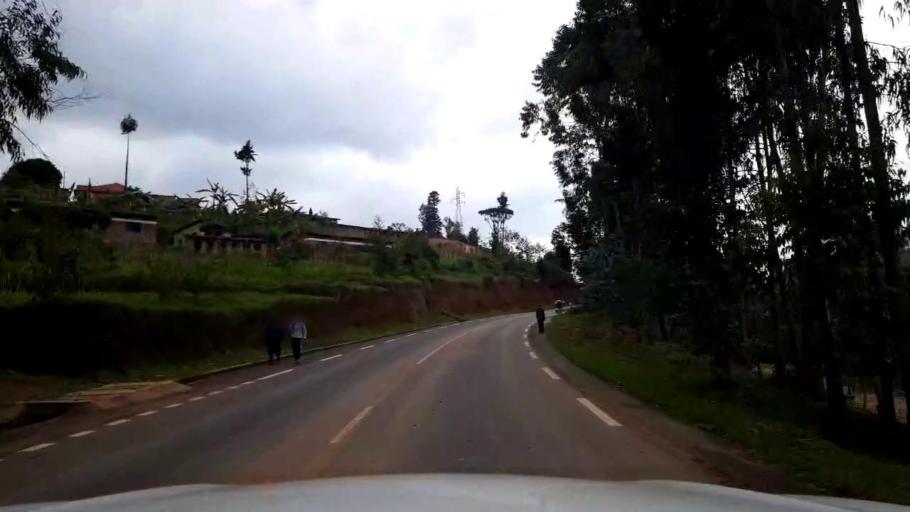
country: RW
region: Western Province
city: Kibuye
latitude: -1.8808
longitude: 29.3510
